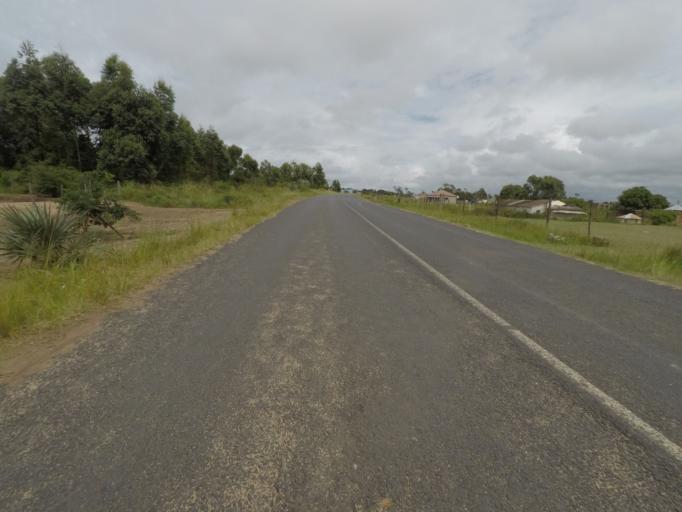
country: ZA
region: KwaZulu-Natal
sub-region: uThungulu District Municipality
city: eSikhawini
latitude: -28.9142
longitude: 31.8503
